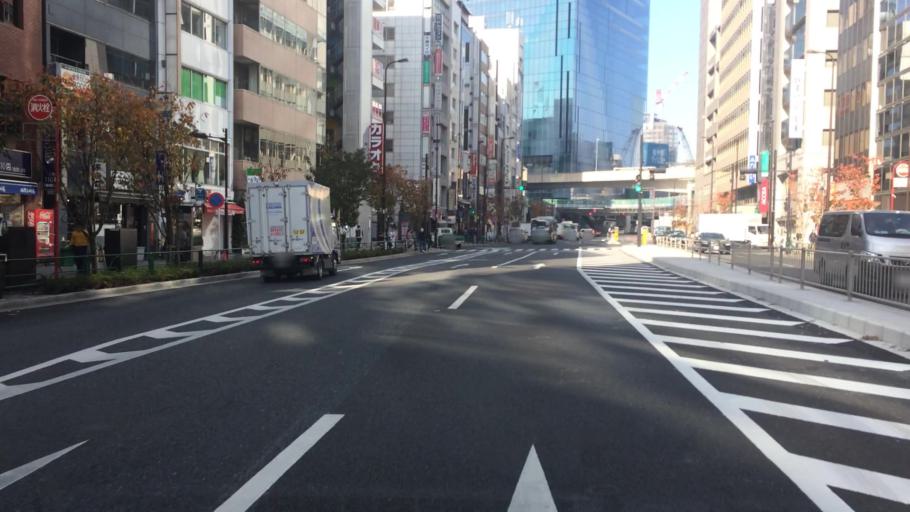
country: JP
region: Tokyo
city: Tokyo
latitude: 35.6566
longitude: 139.7049
